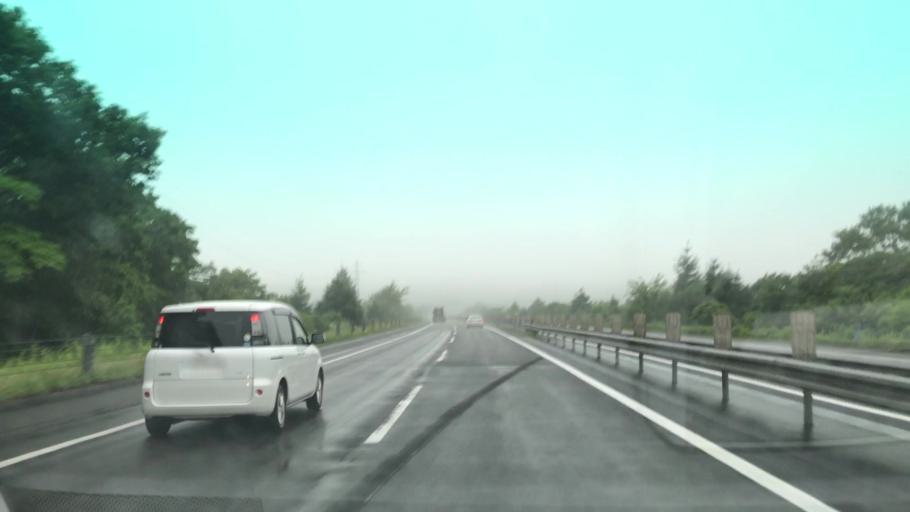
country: JP
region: Hokkaido
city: Tomakomai
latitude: 42.6609
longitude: 141.5802
